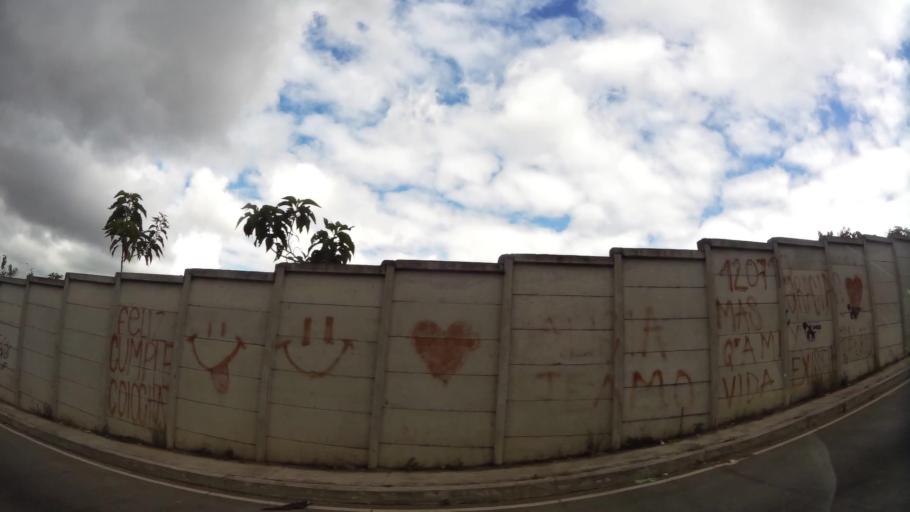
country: GT
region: Guatemala
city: Guatemala City
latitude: 14.6655
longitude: -90.5518
